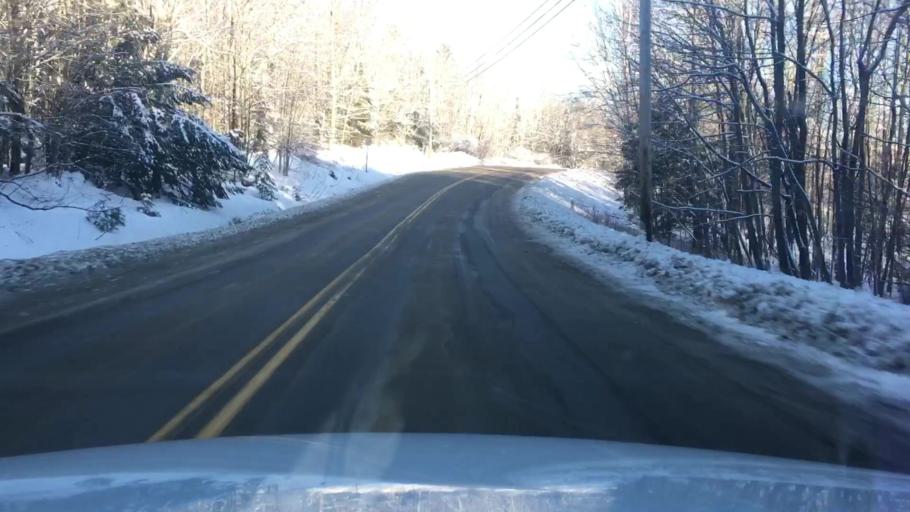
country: US
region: Maine
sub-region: Kennebec County
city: Mount Vernon
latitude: 44.4684
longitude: -69.9745
